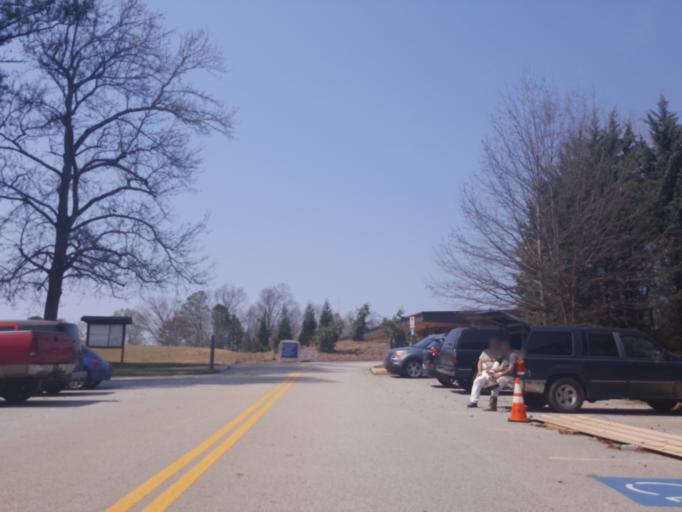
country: US
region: Georgia
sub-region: Carroll County
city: Carrollton
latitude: 33.5732
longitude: -85.1081
